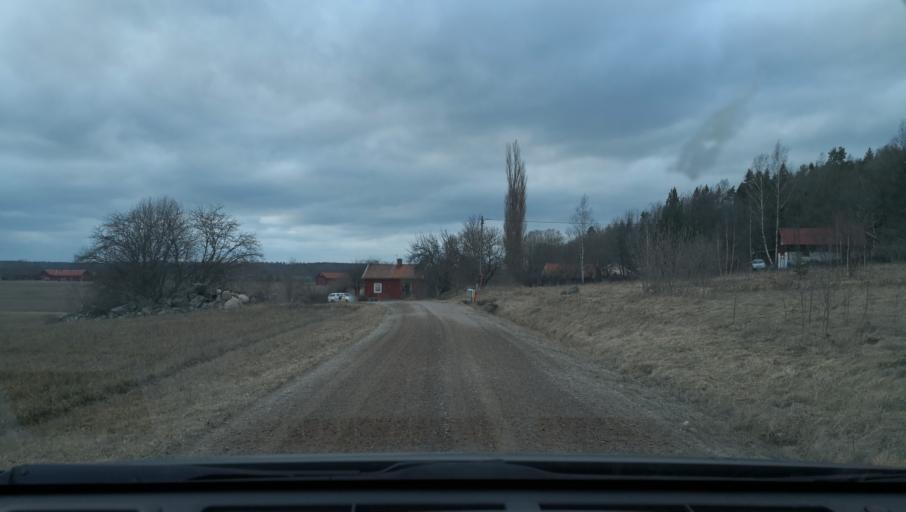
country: SE
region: Vaestmanland
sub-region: Kopings Kommun
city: Koping
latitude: 59.5323
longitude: 15.9036
